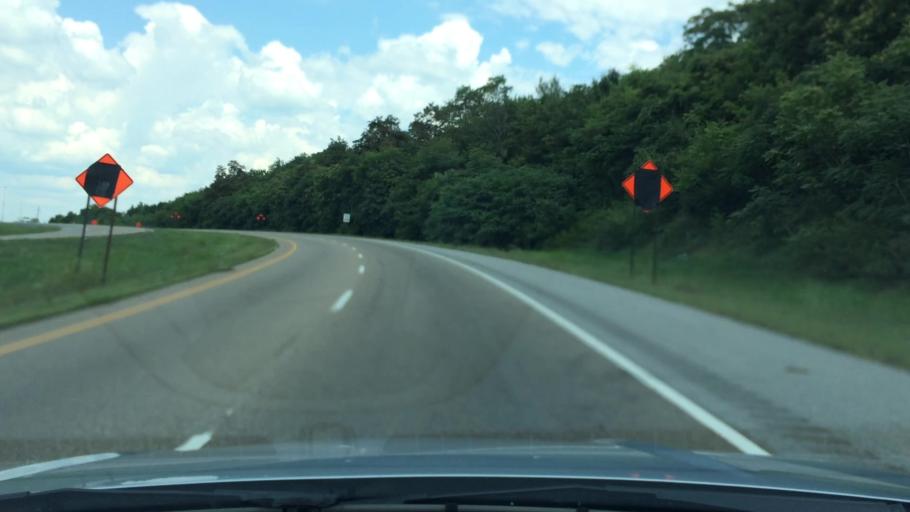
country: US
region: Tennessee
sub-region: Hamblen County
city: Morristown
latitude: 36.1694
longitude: -83.3535
